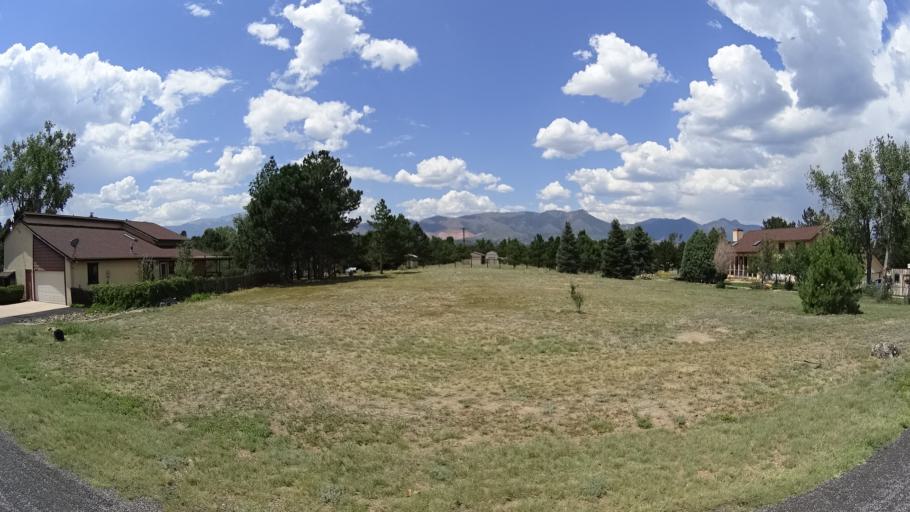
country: US
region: Colorado
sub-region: El Paso County
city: Air Force Academy
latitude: 38.9364
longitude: -104.8060
